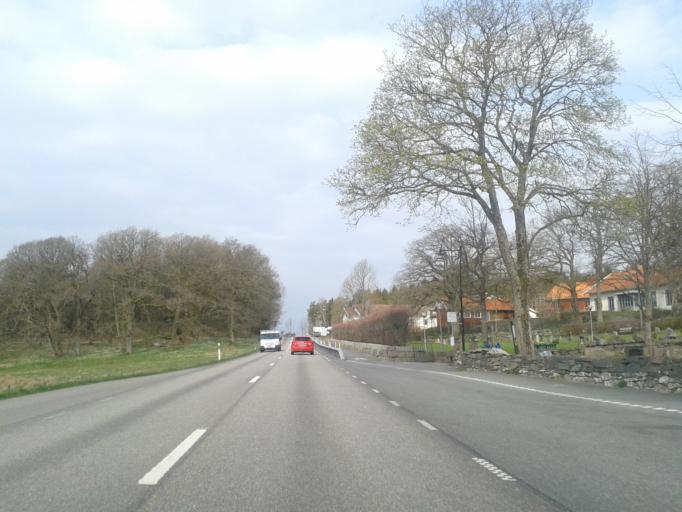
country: SE
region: Vaestra Goetaland
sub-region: Kungalvs Kommun
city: Kode
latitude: 57.8953
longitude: 11.8278
